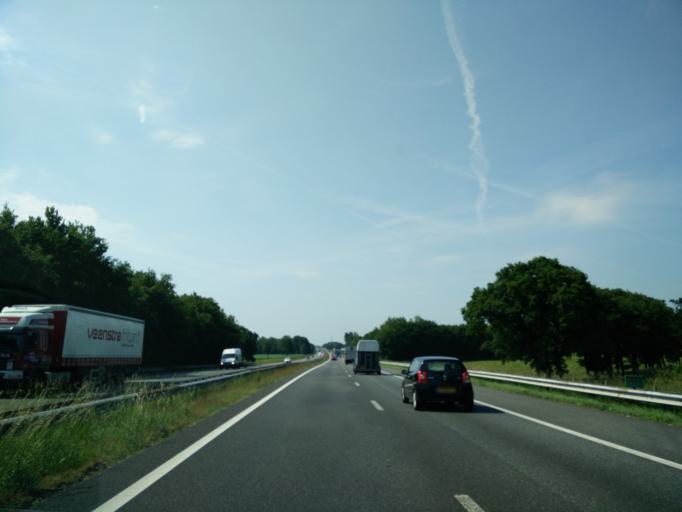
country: NL
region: Drenthe
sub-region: Gemeente Tynaarlo
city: Tynaarlo
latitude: 53.0607
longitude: 6.6008
